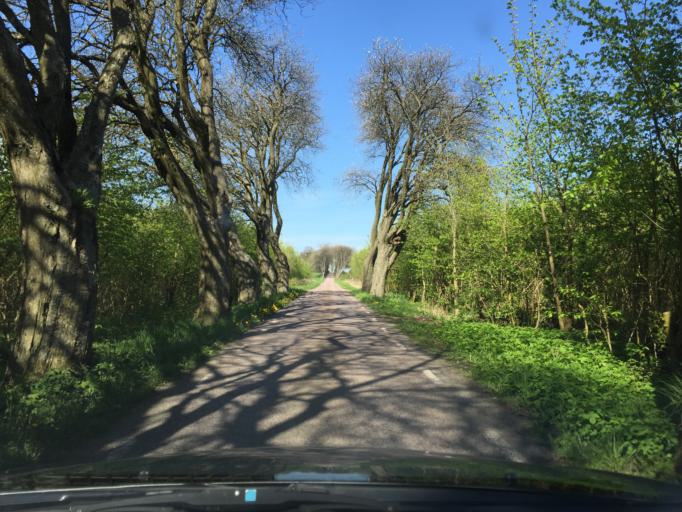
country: SE
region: Skane
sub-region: Sjobo Kommun
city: Blentarp
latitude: 55.5584
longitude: 13.5365
